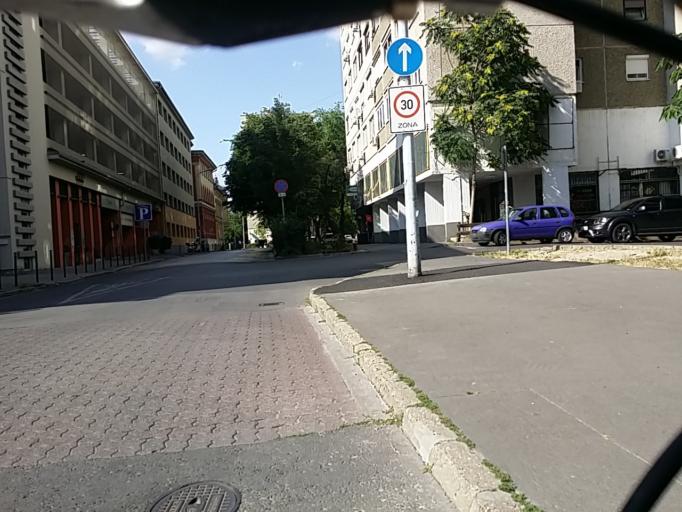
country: HU
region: Budapest
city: Budapest III. keruelet
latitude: 47.5405
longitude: 19.0432
